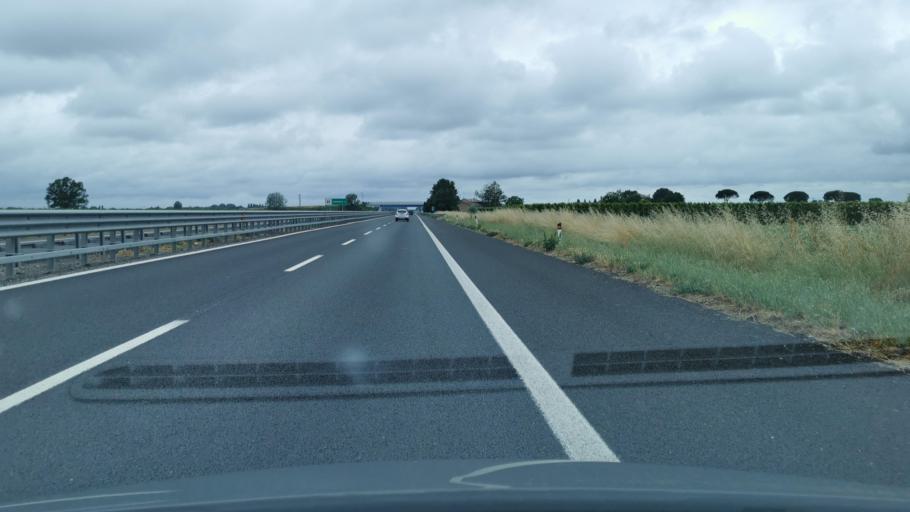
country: IT
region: Emilia-Romagna
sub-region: Provincia di Ravenna
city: Godo
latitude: 44.4001
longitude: 12.0607
